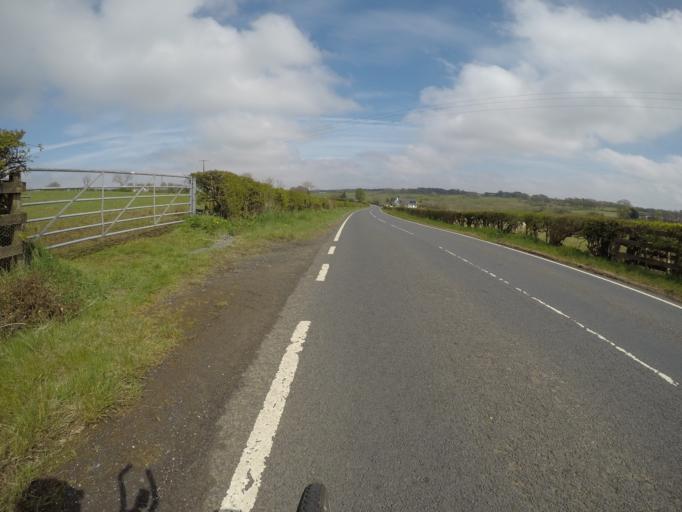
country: GB
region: Scotland
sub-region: East Ayrshire
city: Stewarton
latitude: 55.7049
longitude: -4.4681
